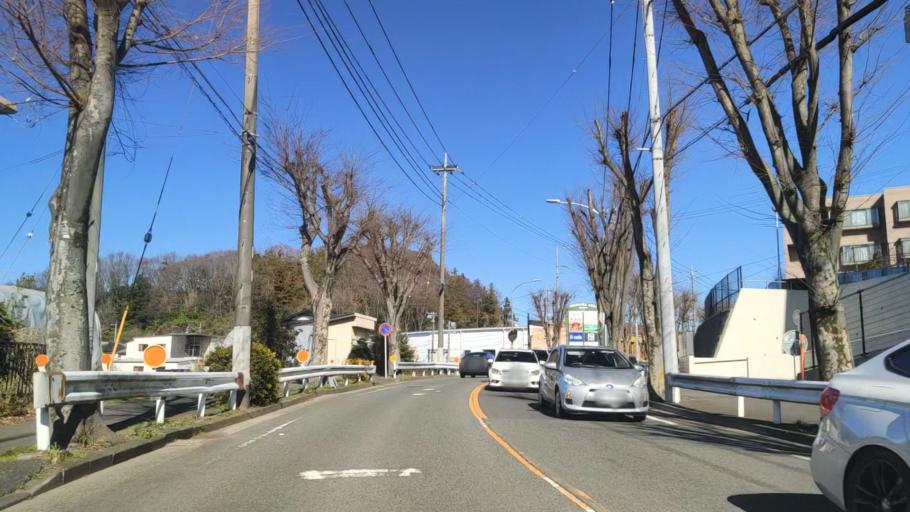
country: JP
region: Tokyo
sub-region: Machida-shi
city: Machida
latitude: 35.5451
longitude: 139.4988
